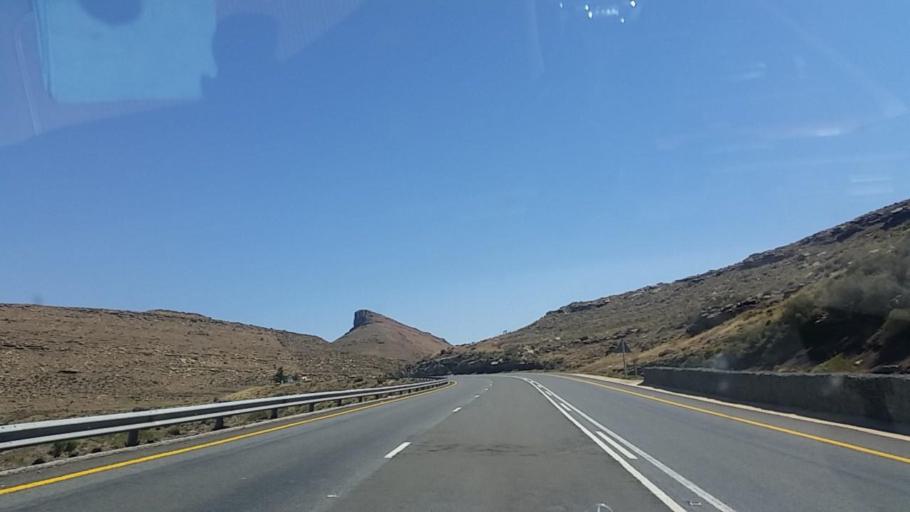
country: ZA
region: Eastern Cape
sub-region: Chris Hani District Municipality
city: Middelburg
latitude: -31.8382
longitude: 24.8624
